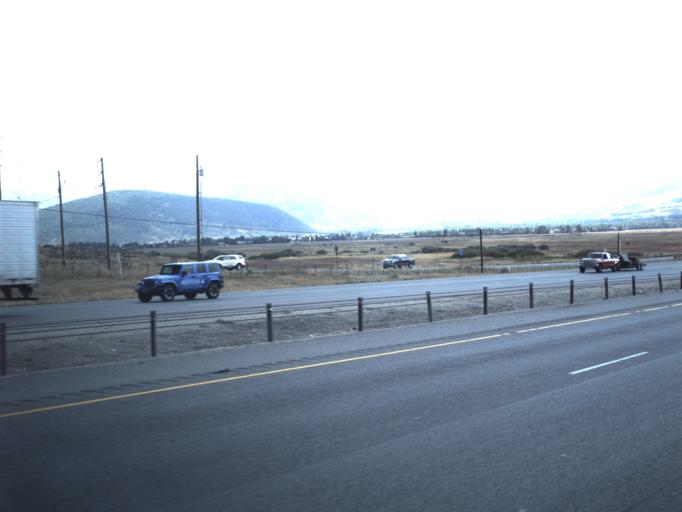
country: US
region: Utah
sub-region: Summit County
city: Snyderville
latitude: 40.7233
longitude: -111.5159
